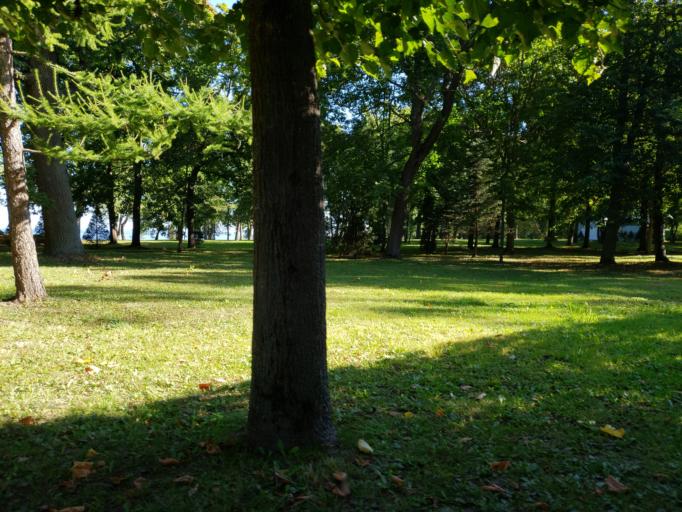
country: RU
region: St.-Petersburg
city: Peterhof
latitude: 59.8880
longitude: 29.9052
